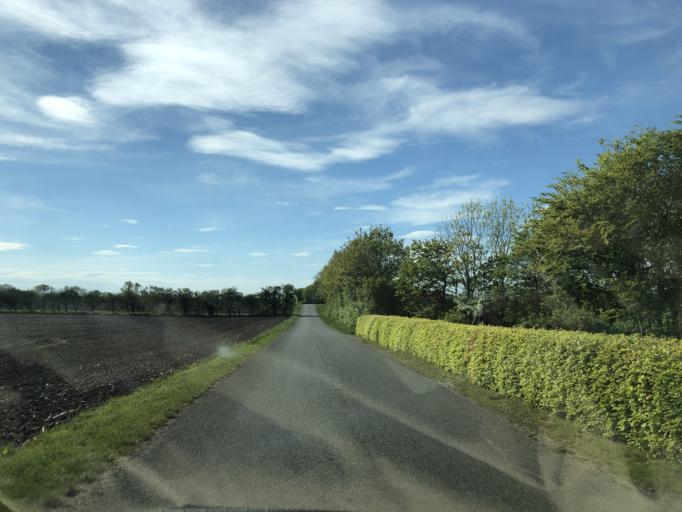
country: DK
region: Central Jutland
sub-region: Ringkobing-Skjern Kommune
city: Videbaek
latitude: 56.0924
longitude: 8.4953
